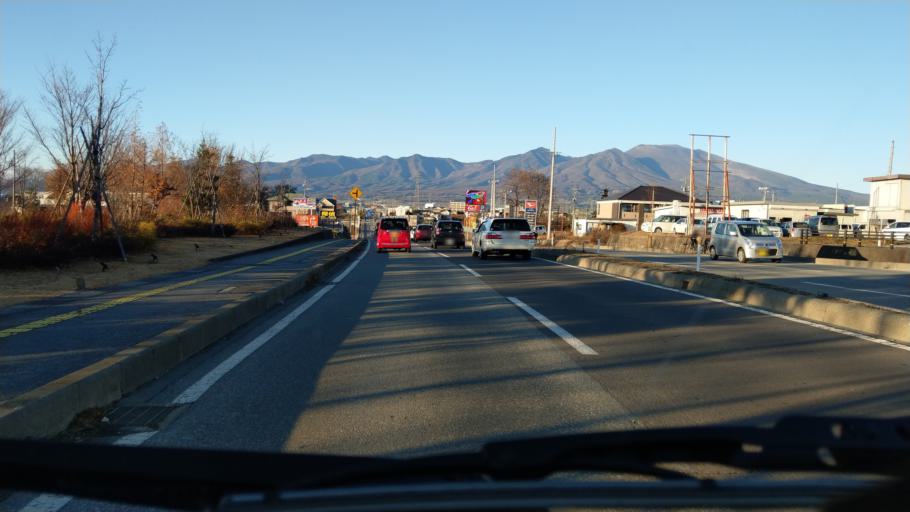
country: JP
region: Nagano
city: Saku
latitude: 36.2585
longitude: 138.4678
